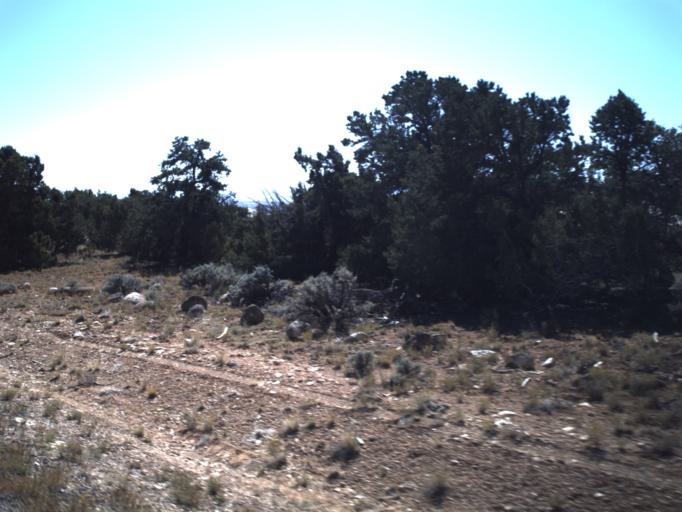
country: US
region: Utah
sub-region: Wayne County
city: Loa
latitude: 37.8771
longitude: -111.4532
